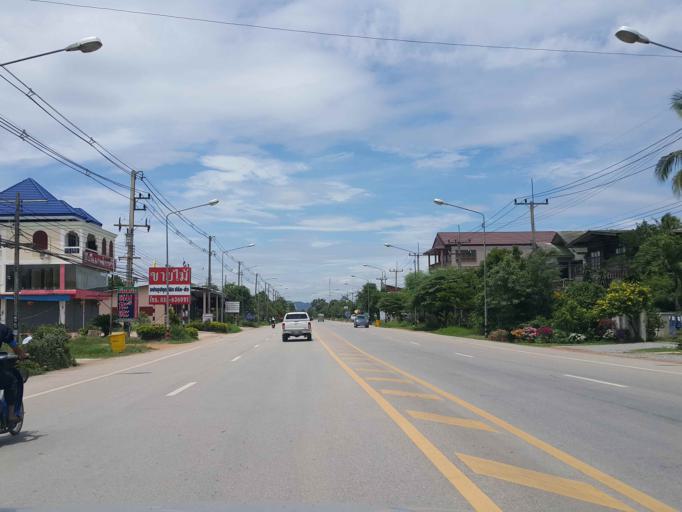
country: TH
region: Sukhothai
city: Ban Na
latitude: 17.0137
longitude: 99.7584
